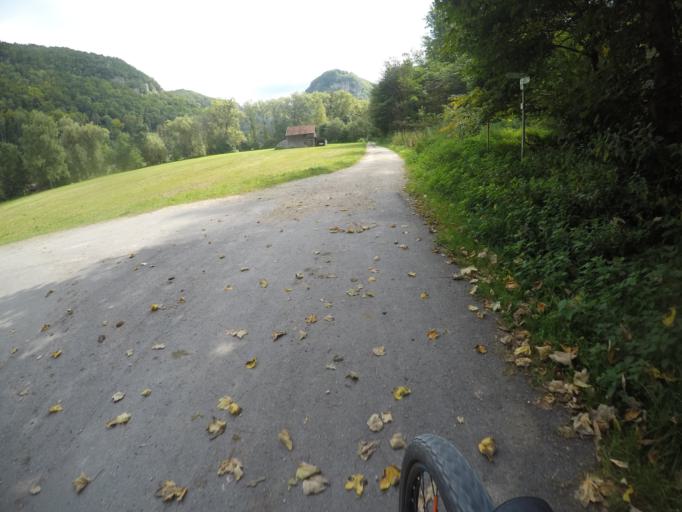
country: DE
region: Baden-Wuerttemberg
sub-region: Tuebingen Region
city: Bad Urach
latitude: 48.4719
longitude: 9.4133
